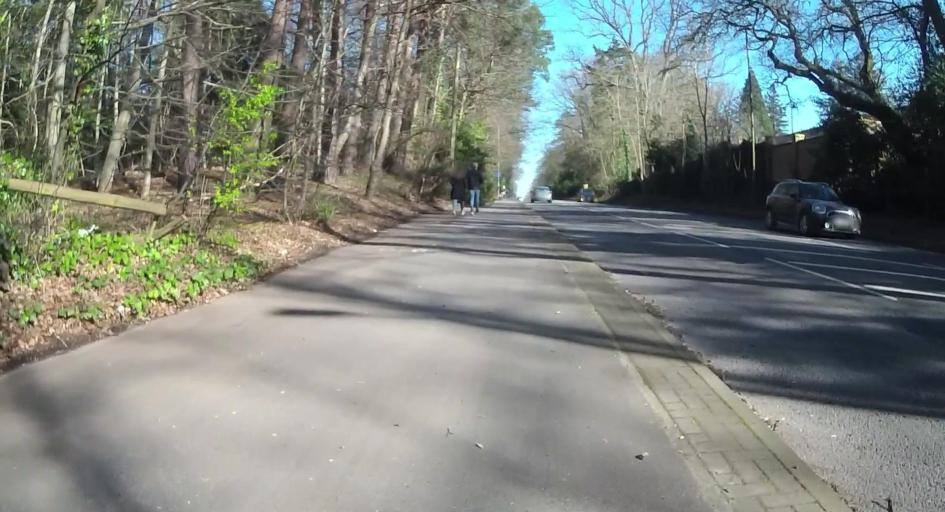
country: GB
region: England
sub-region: Bracknell Forest
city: Warfield
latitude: 51.4124
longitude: -0.7124
